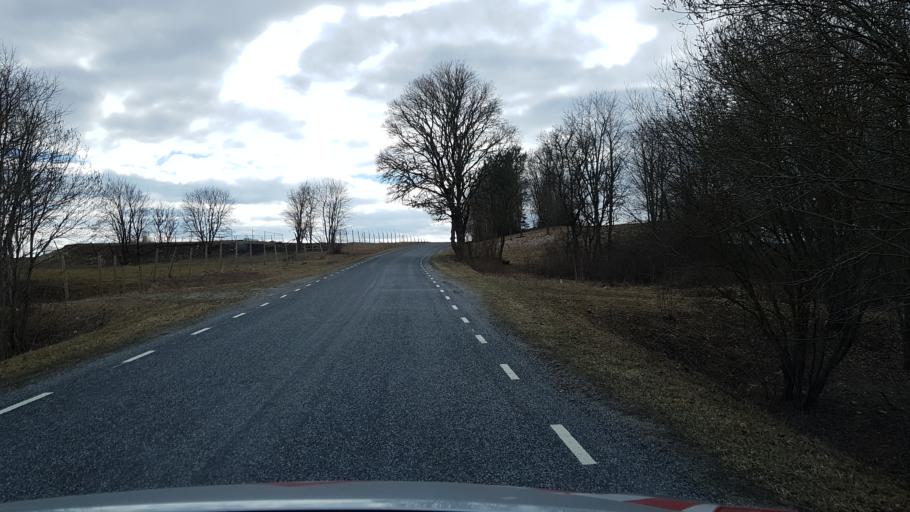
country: EE
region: Laeaene-Virumaa
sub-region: Tamsalu vald
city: Tamsalu
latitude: 59.2085
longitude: 26.1465
